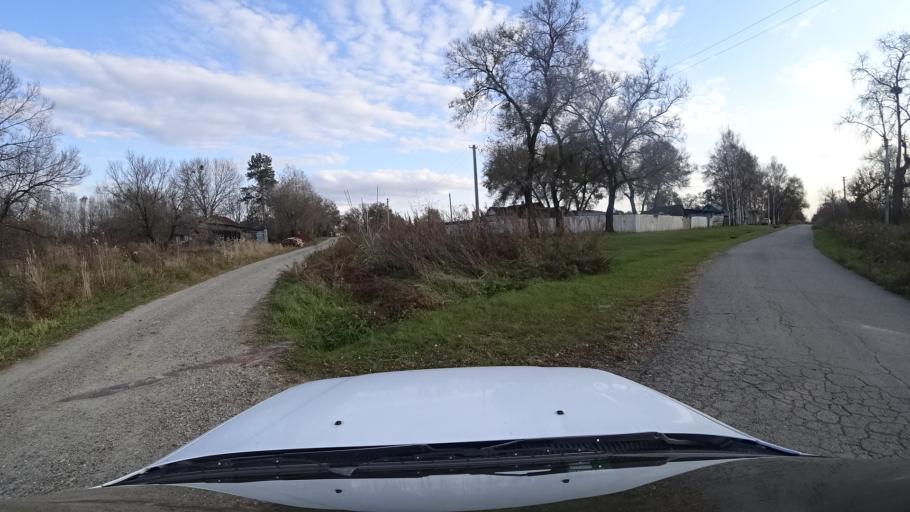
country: RU
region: Primorskiy
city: Lazo
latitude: 45.8226
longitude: 133.6148
